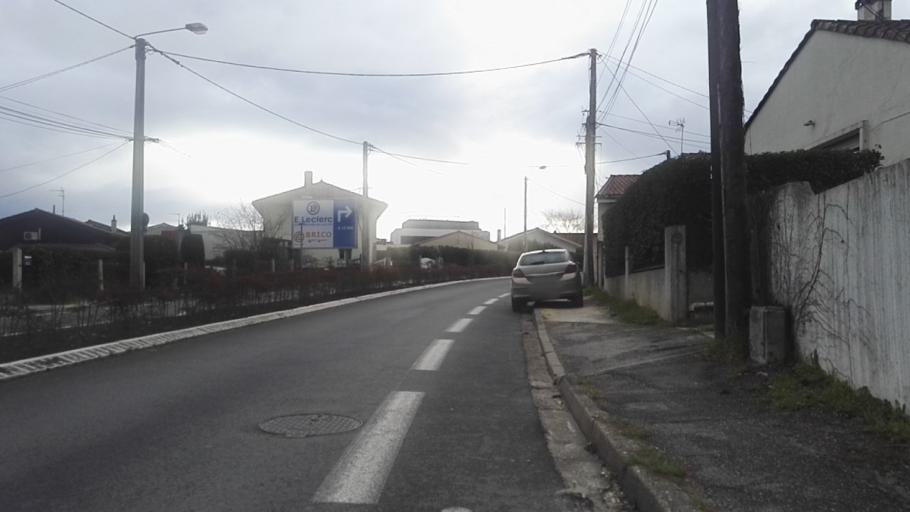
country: FR
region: Aquitaine
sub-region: Departement de la Gironde
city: Eysines
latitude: 44.8626
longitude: -0.6400
